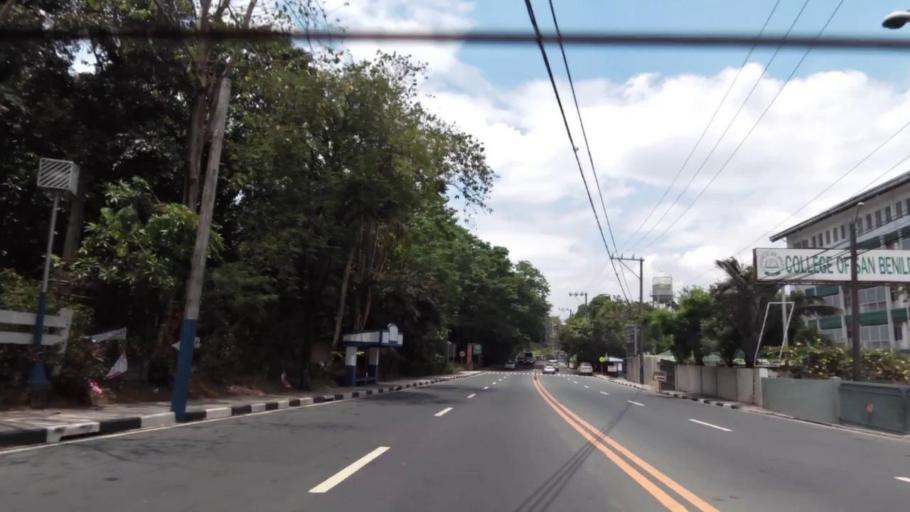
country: PH
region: Calabarzon
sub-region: Province of Rizal
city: Antipolo
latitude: 14.6192
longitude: 121.1487
